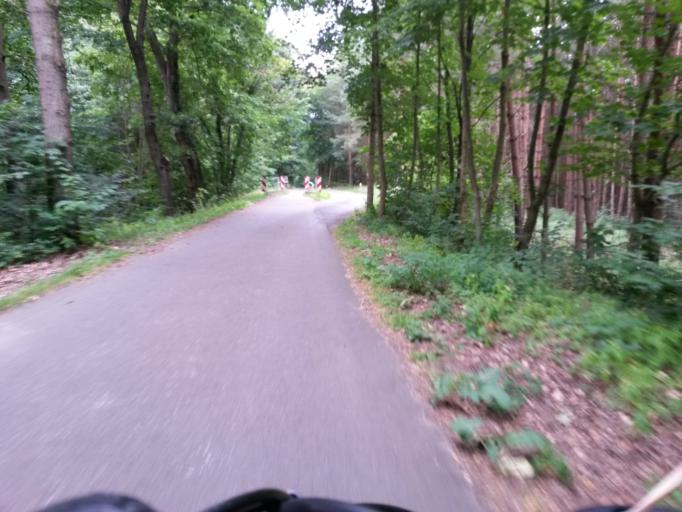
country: DE
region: Brandenburg
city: Angermunde
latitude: 53.0504
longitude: 13.9423
